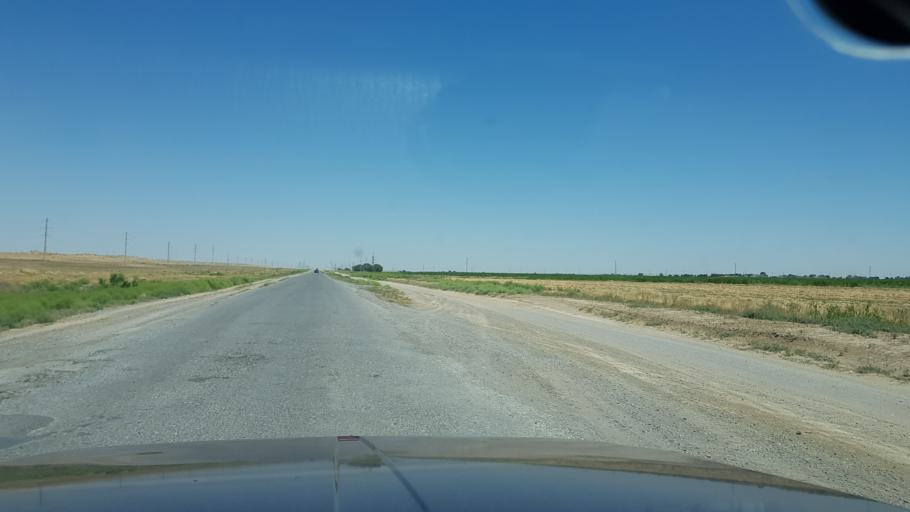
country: TM
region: Ahal
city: Annau
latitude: 37.8614
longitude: 58.7103
